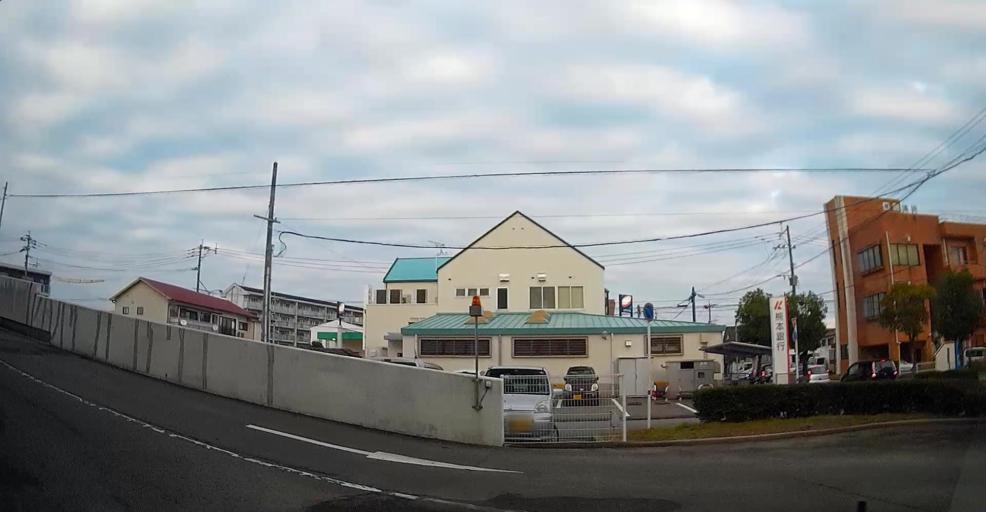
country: JP
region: Kumamoto
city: Hondo
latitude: 32.4557
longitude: 130.1930
